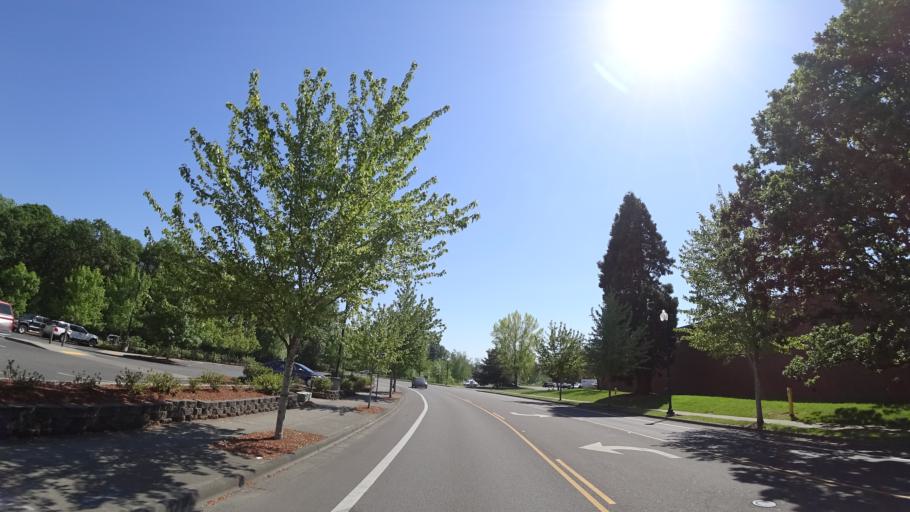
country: US
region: Oregon
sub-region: Washington County
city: Beaverton
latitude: 45.4994
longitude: -122.8137
